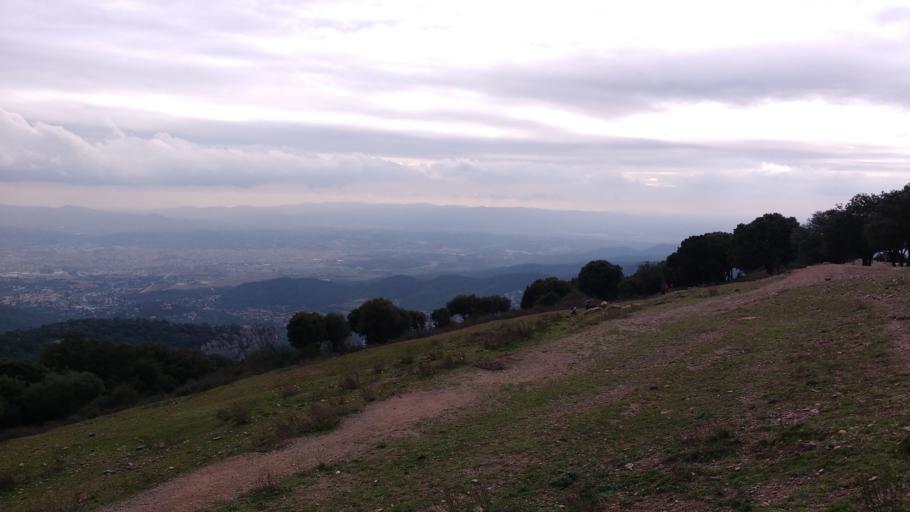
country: ES
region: Catalonia
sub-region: Provincia de Barcelona
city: Matadepera
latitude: 41.6405
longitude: 2.0178
